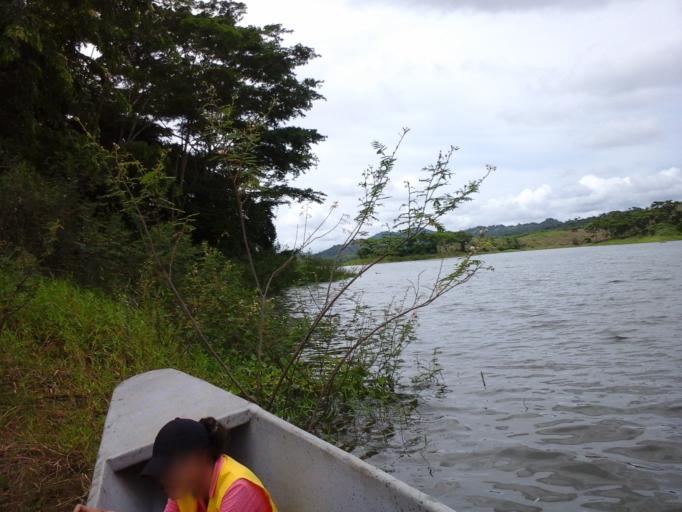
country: CO
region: Bolivar
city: San Cristobal
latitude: 9.8734
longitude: -75.3009
